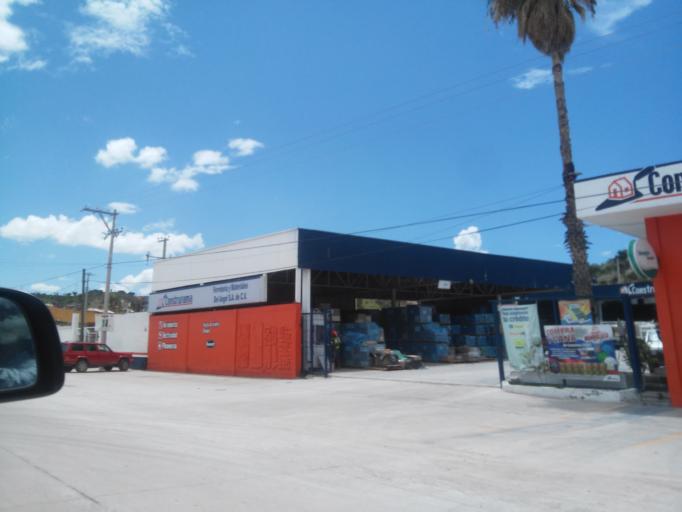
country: MX
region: Durango
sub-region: Santiago Papasquiaro
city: Santiago Papasquiaro
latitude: 25.0546
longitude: -105.4248
